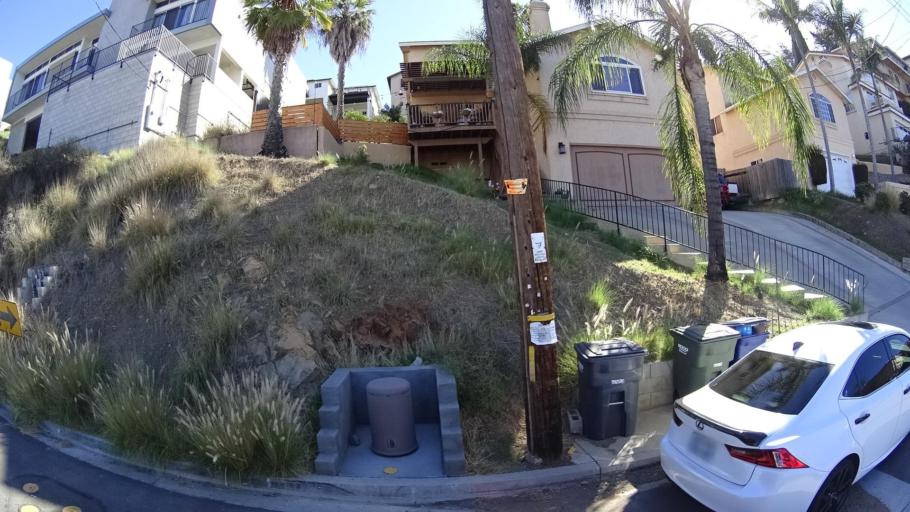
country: US
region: California
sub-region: San Diego County
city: La Presa
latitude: 32.7165
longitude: -116.9874
